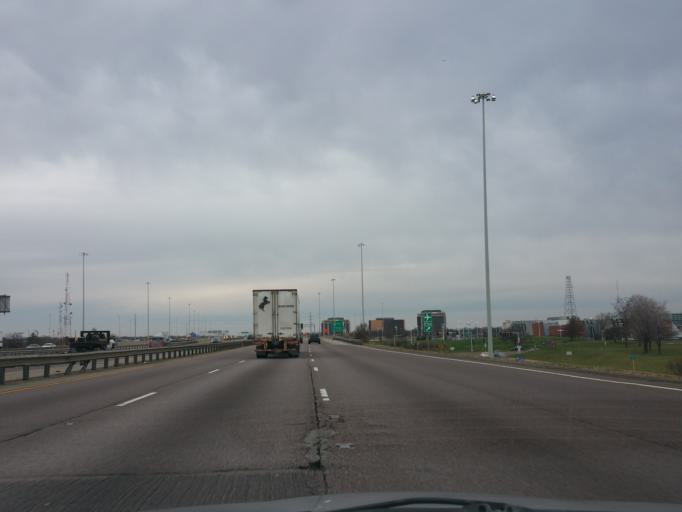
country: US
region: Illinois
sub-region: Cook County
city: Rolling Meadows
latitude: 42.0483
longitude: -88.0292
